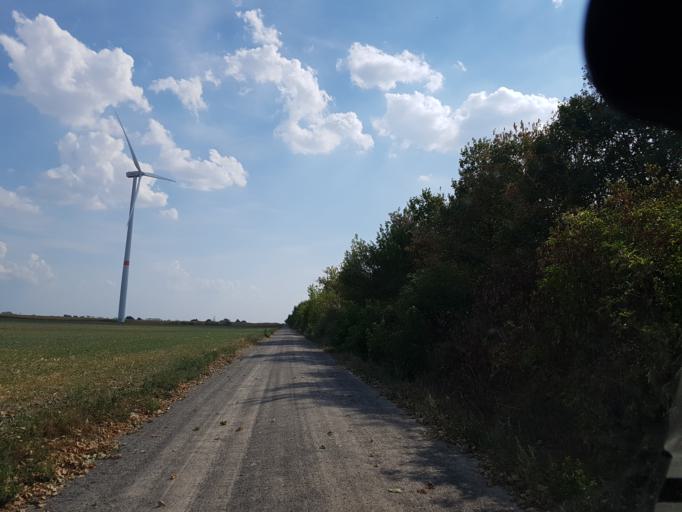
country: DE
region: Brandenburg
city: Treuenbrietzen
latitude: 52.0083
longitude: 12.8688
